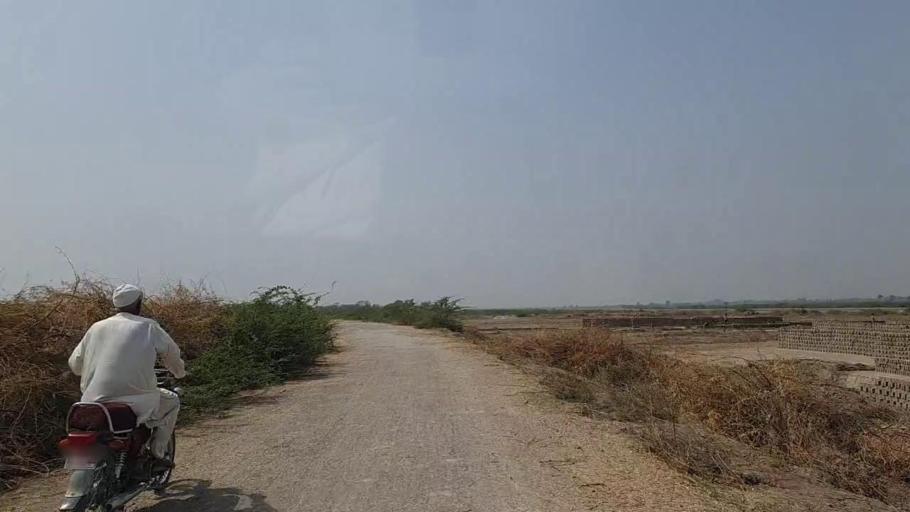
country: PK
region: Sindh
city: Naukot
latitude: 24.8299
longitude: 69.3860
